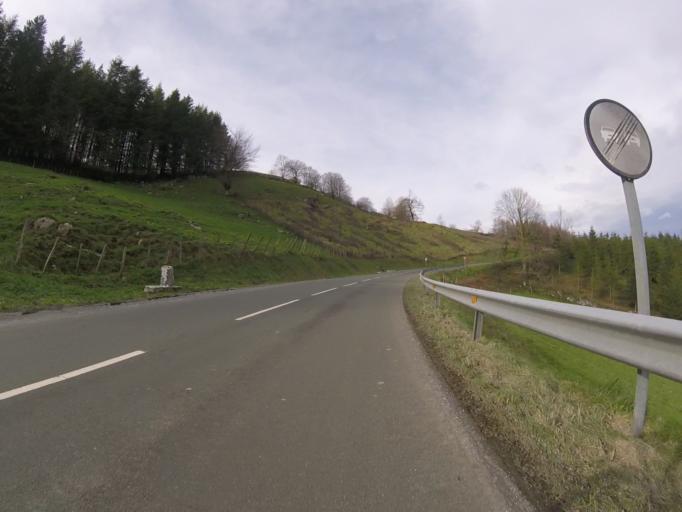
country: ES
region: Basque Country
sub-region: Provincia de Guipuzcoa
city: Errezil
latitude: 43.1487
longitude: -2.1856
